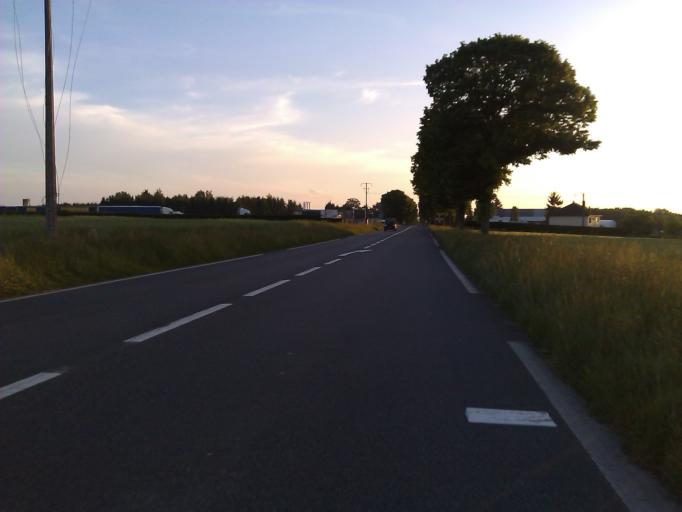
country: FR
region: Poitou-Charentes
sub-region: Departement de la Vienne
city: Saint-Savin
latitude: 46.5698
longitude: 0.8892
